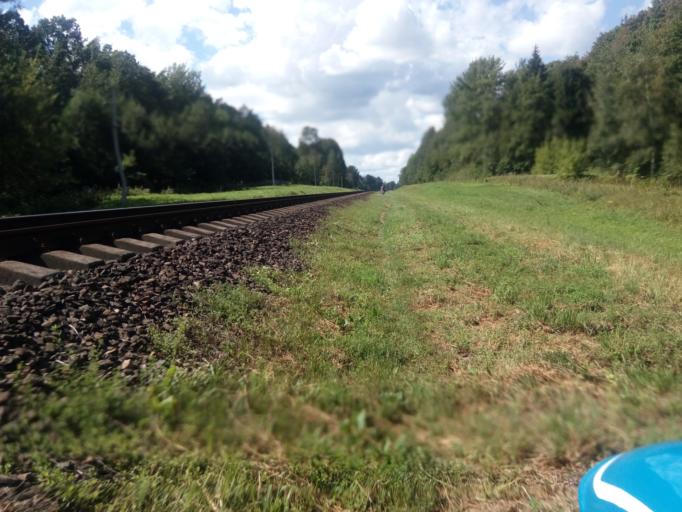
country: BY
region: Vitebsk
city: Dzisna
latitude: 55.6773
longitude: 28.3037
